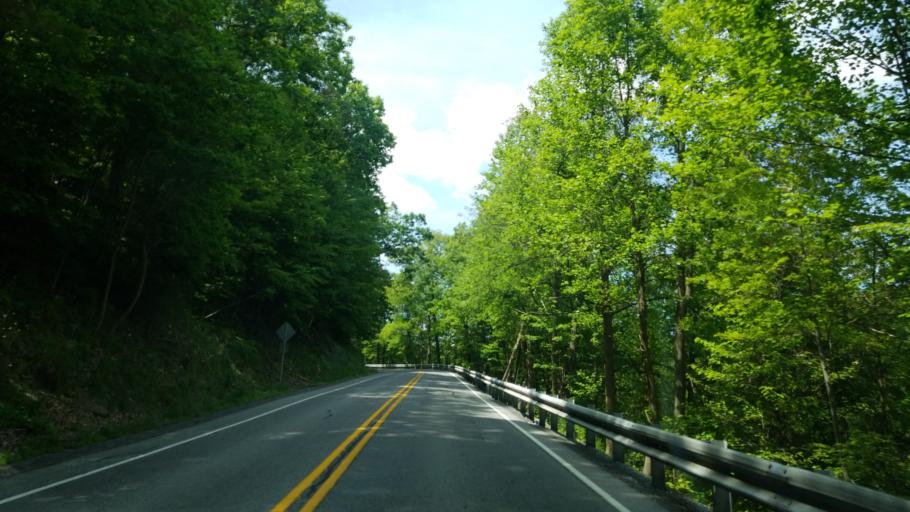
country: US
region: Pennsylvania
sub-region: Blair County
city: Tyrone
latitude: 40.6949
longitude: -78.2813
